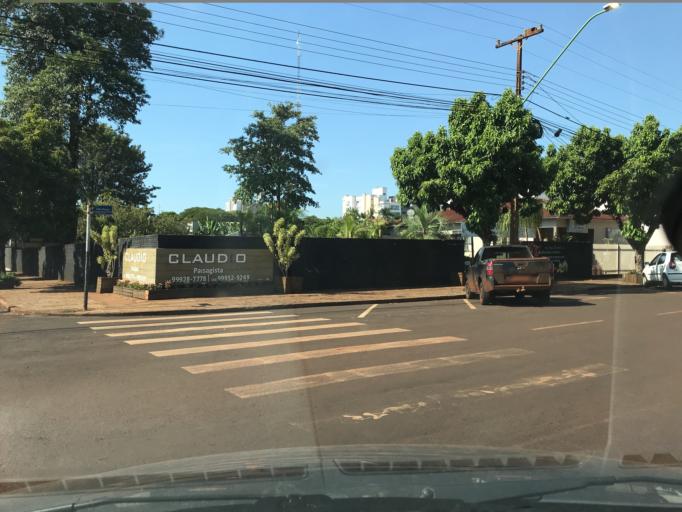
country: BR
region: Parana
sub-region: Palotina
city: Palotina
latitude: -24.2837
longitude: -53.8374
